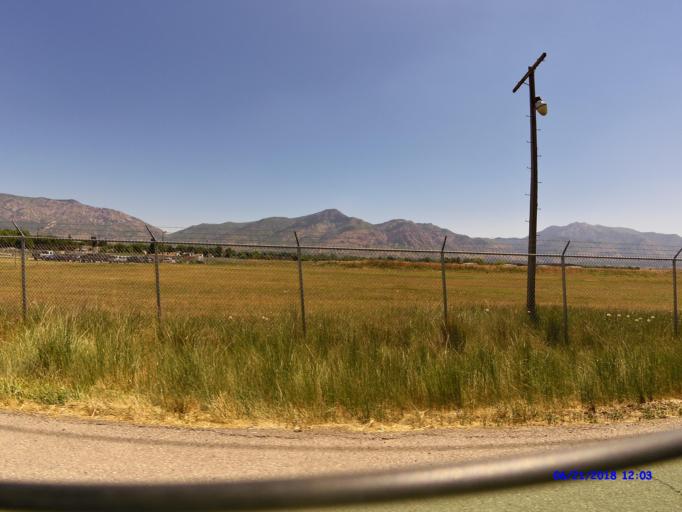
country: US
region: Utah
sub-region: Weber County
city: Harrisville
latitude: 41.2816
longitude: -112.0084
